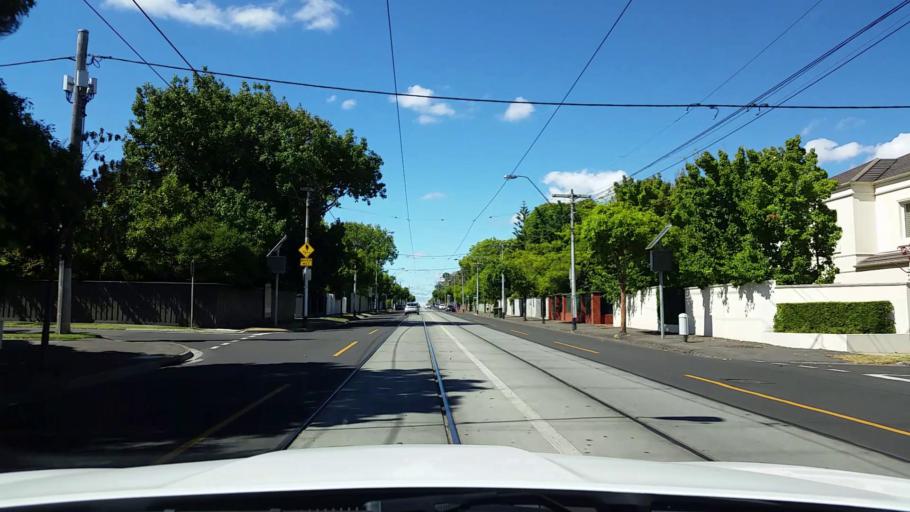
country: AU
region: Victoria
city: Toorak
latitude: -37.8506
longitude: 145.0226
